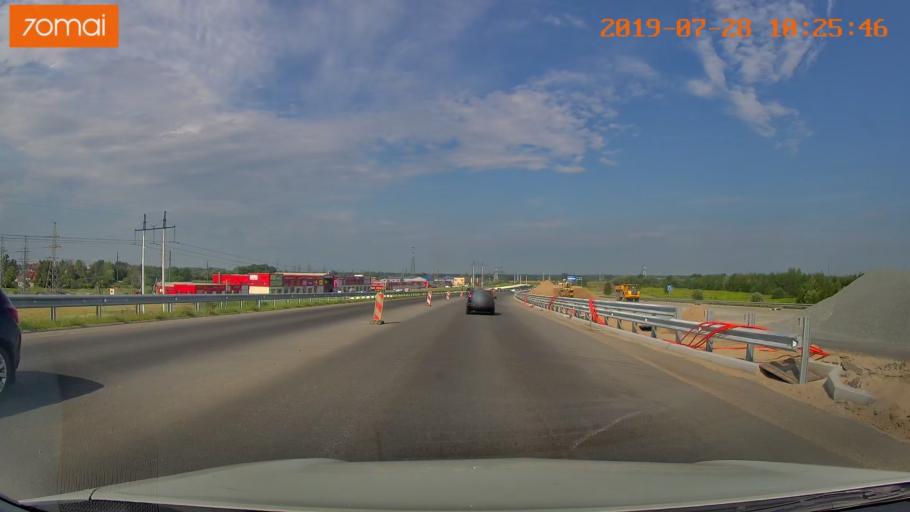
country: RU
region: Kaliningrad
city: Maloye Isakovo
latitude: 54.7679
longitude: 20.5375
